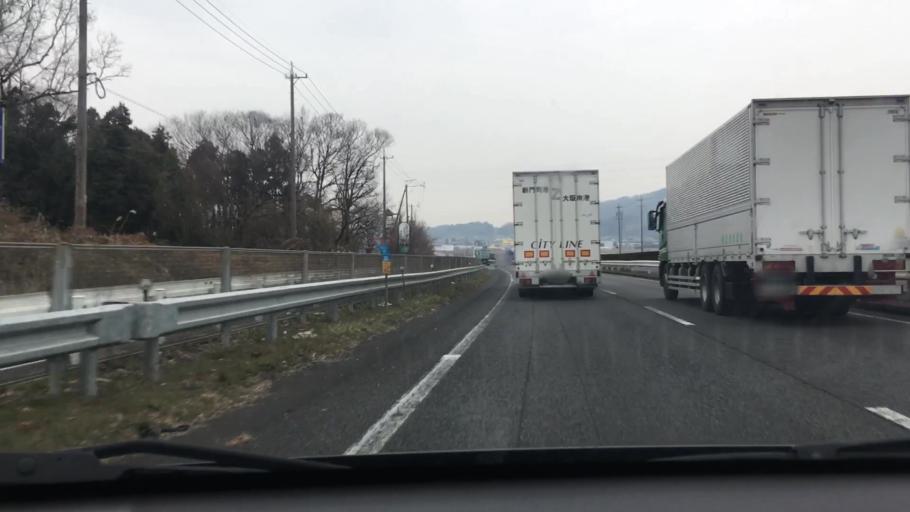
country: JP
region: Mie
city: Ueno-ebisumachi
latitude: 34.7641
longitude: 136.1554
